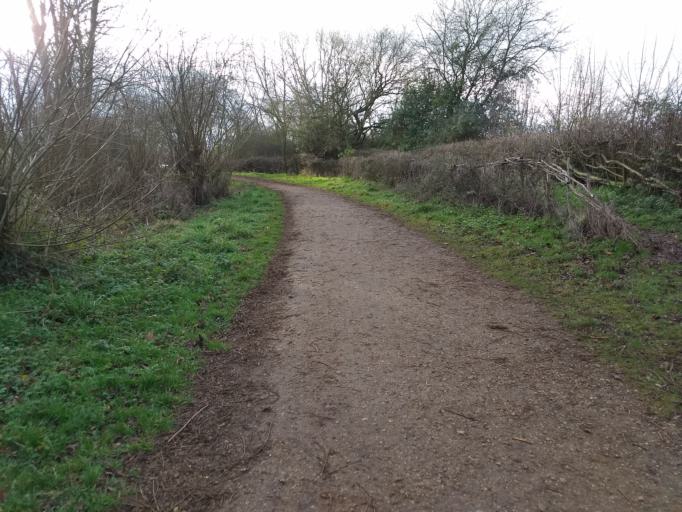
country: GB
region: England
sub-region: Bedford
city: Odell
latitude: 52.2064
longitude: -0.5946
